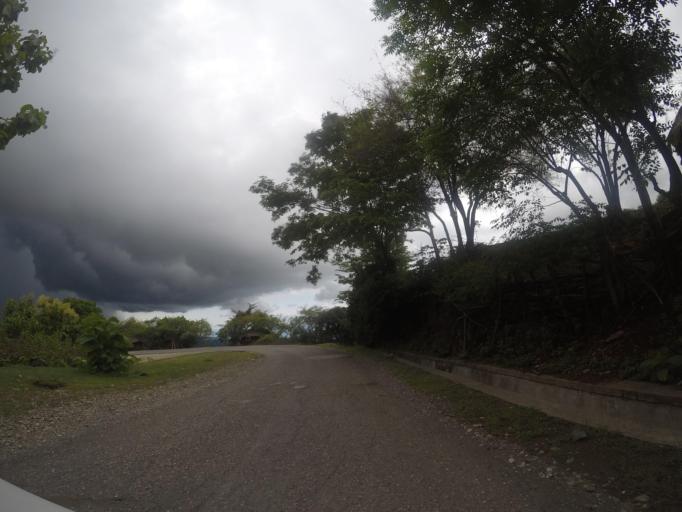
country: ID
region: East Nusa Tenggara
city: Atambua
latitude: -8.9630
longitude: 125.0217
